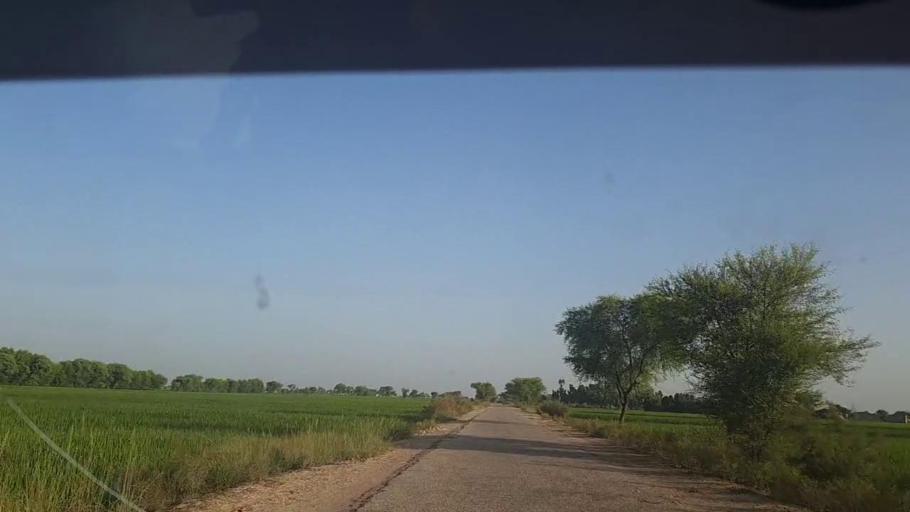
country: PK
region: Sindh
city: Thul
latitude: 28.2086
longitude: 68.8706
